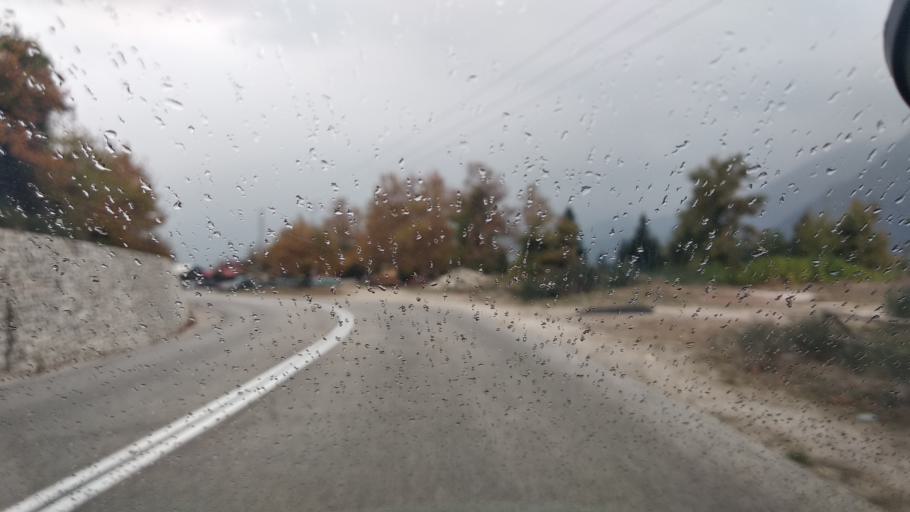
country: GR
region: Thessaly
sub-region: Trikala
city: Pyli
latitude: 39.4942
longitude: 21.5403
